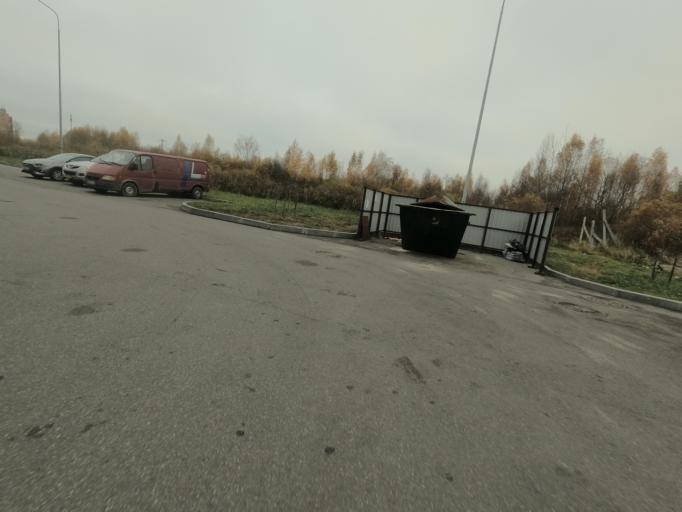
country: RU
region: Leningrad
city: Kirovsk
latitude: 59.8787
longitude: 31.0065
